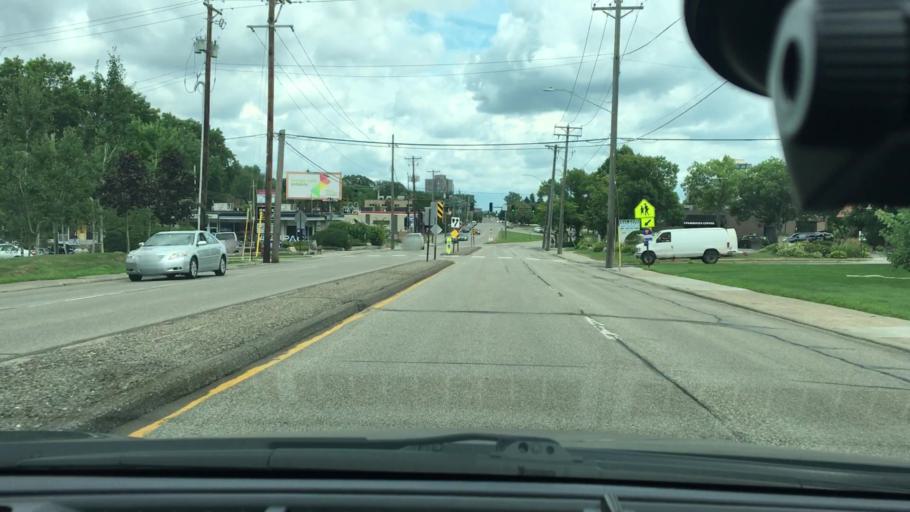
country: US
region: Minnesota
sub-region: Hennepin County
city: Saint Louis Park
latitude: 44.9484
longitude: -93.3346
